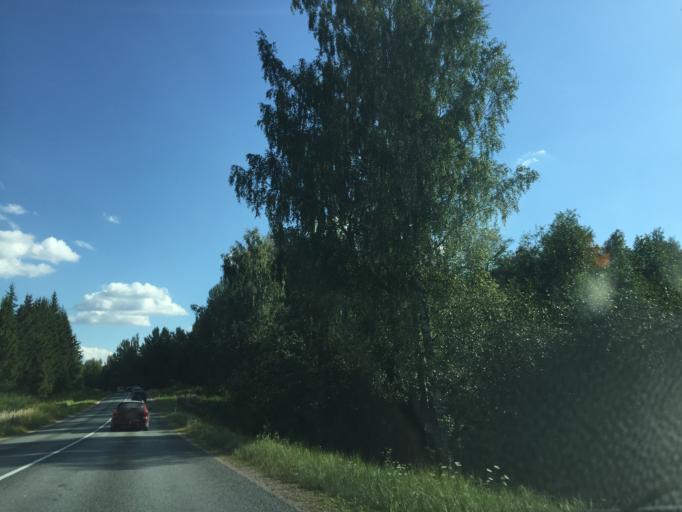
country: LV
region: Beverina
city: Murmuiza
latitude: 57.4469
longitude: 25.4310
